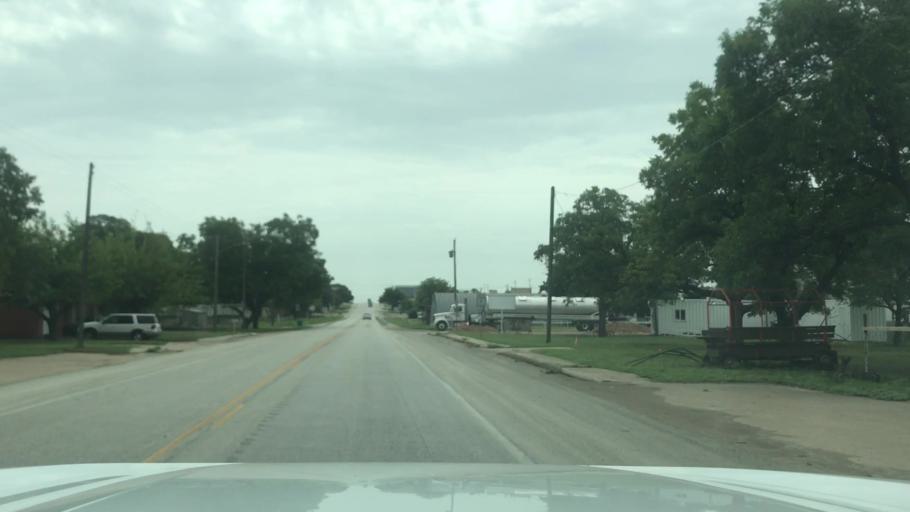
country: US
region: Texas
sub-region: Eastland County
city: Gorman
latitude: 32.2135
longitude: -98.6705
